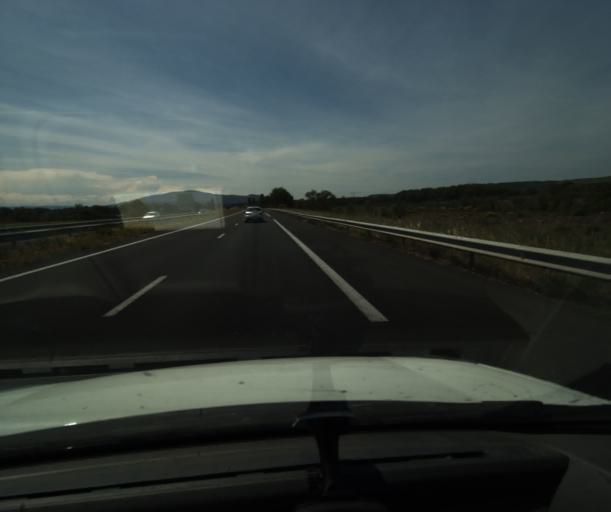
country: FR
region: Languedoc-Roussillon
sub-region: Departement de l'Aude
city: Lezignan-Corbieres
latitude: 43.1705
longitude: 2.7545
